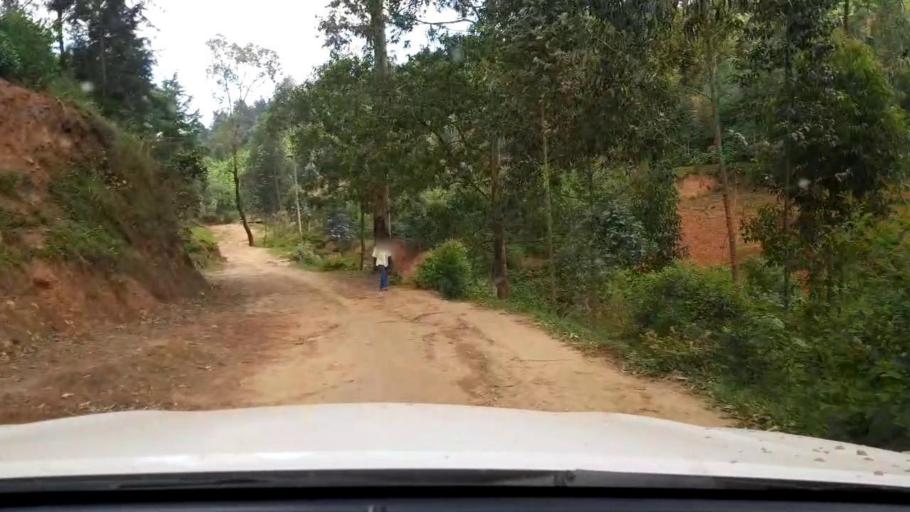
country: RW
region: Western Province
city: Kibuye
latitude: -2.0026
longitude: 29.3726
